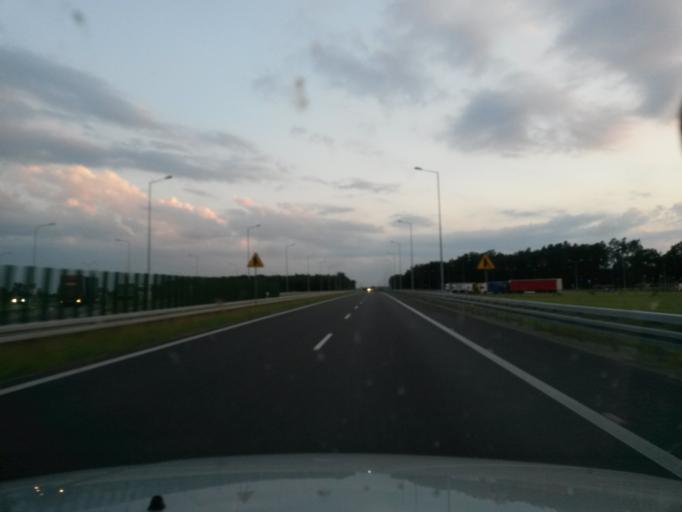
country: PL
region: Lower Silesian Voivodeship
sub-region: Powiat olesnicki
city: Olesnica
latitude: 51.2411
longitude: 17.5016
